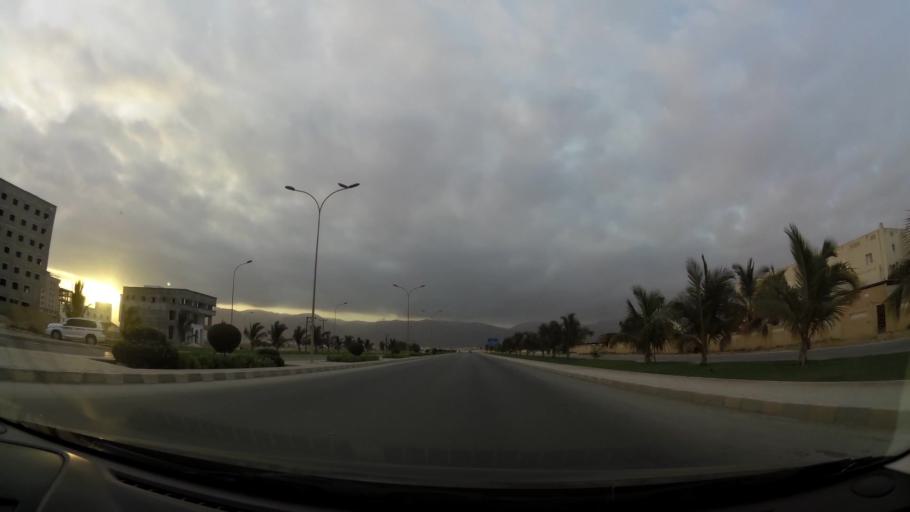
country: OM
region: Zufar
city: Salalah
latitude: 17.0266
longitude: 54.0319
